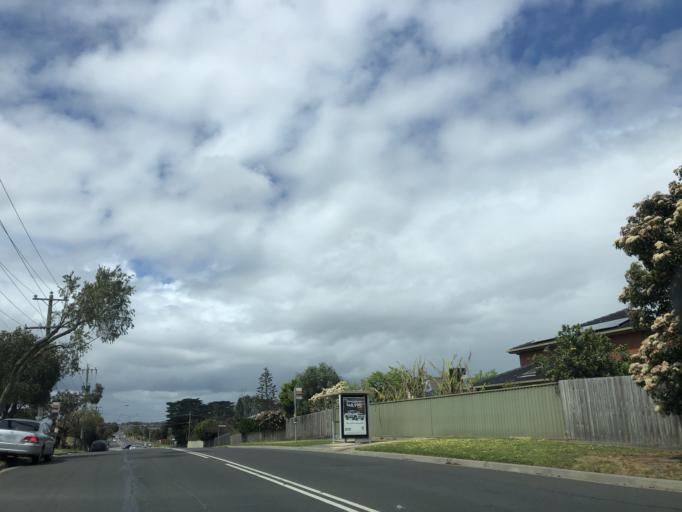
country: AU
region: Victoria
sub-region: Monash
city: Oakleigh South
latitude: -37.9403
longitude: 145.0952
